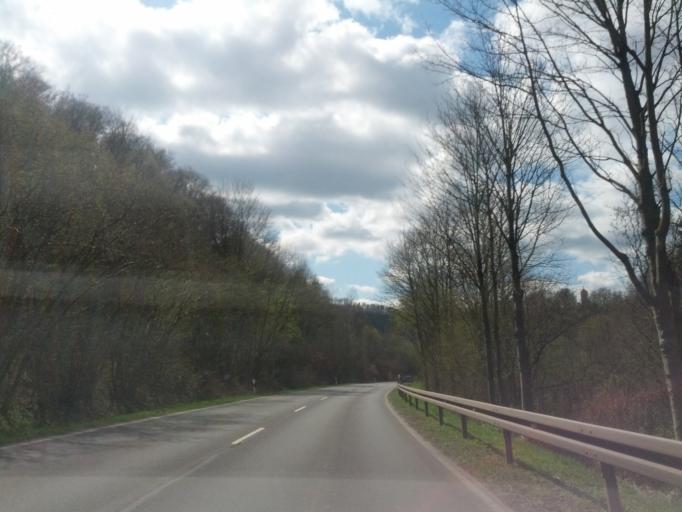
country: DE
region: Thuringia
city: Seebach
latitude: 50.9163
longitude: 10.4093
